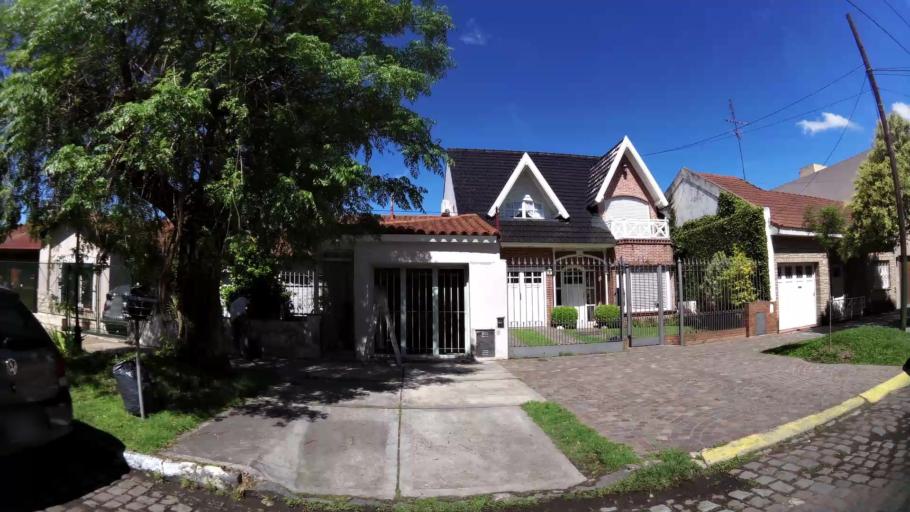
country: AR
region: Buenos Aires
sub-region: Partido de Lomas de Zamora
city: Lomas de Zamora
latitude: -34.7400
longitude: -58.4043
